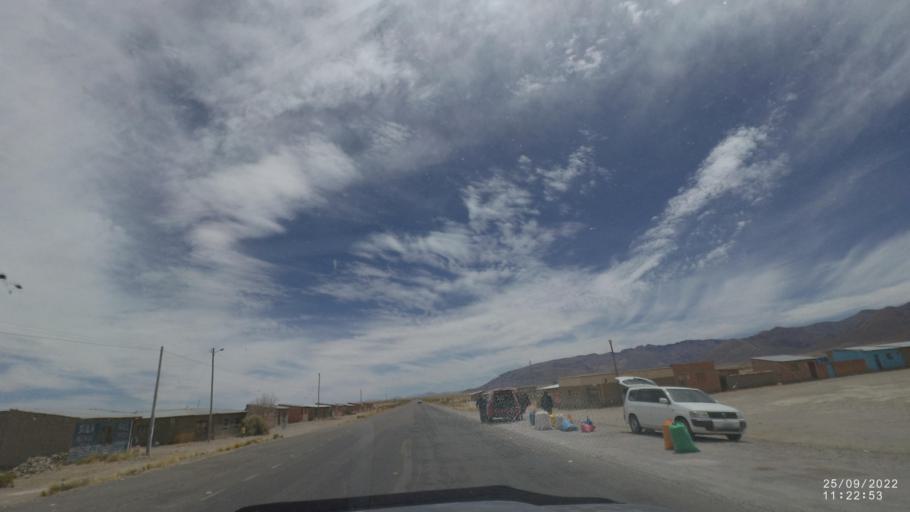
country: BO
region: Oruro
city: Challapata
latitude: -19.1187
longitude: -66.7696
